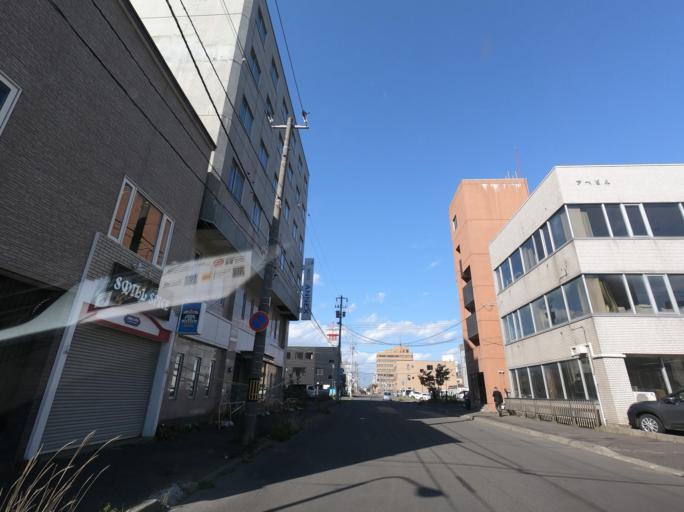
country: JP
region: Hokkaido
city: Kushiro
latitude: 42.9825
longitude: 144.3833
